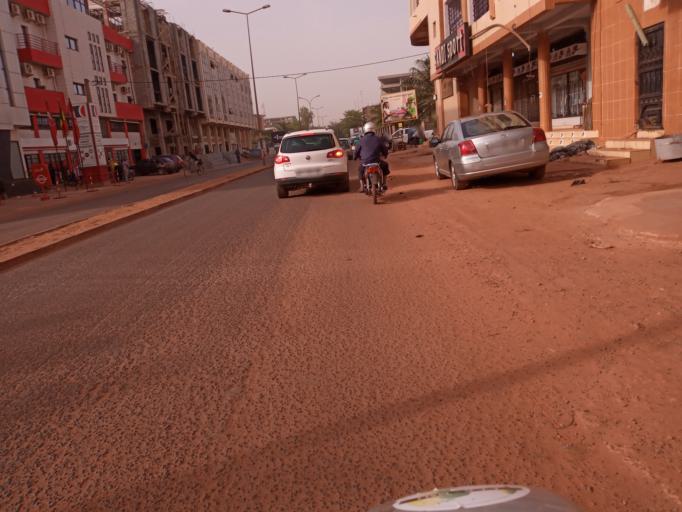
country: ML
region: Bamako
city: Bamako
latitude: 12.6379
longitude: -8.0227
